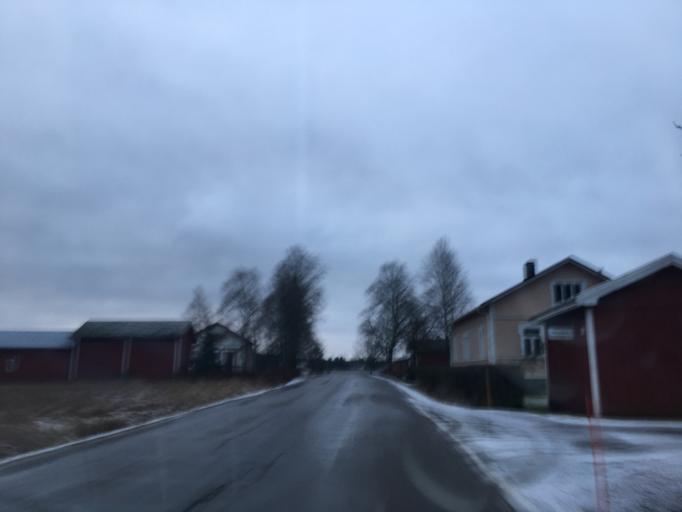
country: FI
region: Varsinais-Suomi
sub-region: Loimaa
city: Aura
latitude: 60.6248
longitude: 22.5827
